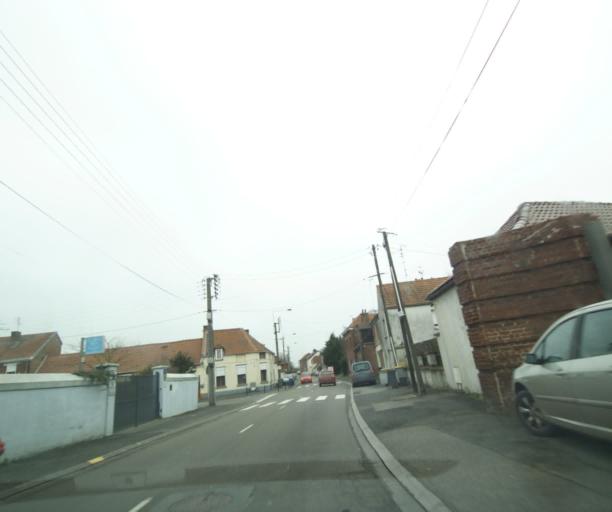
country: FR
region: Nord-Pas-de-Calais
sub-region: Departement du Nord
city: Crespin
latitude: 50.4238
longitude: 3.6607
